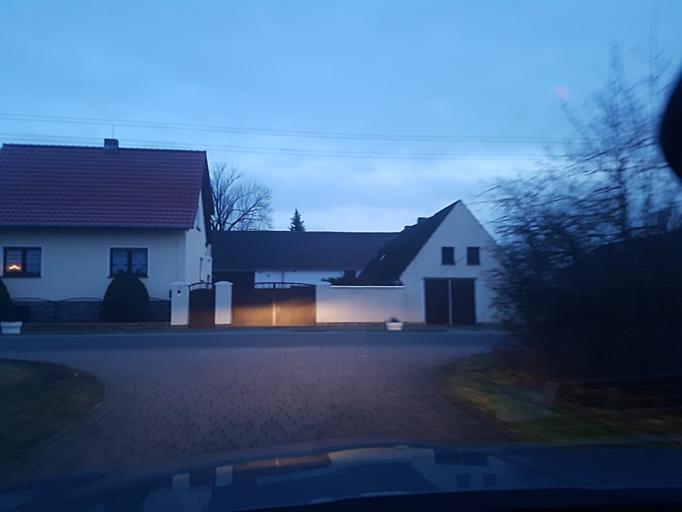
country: DE
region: Brandenburg
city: Ruckersdorf
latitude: 51.5921
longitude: 13.5402
